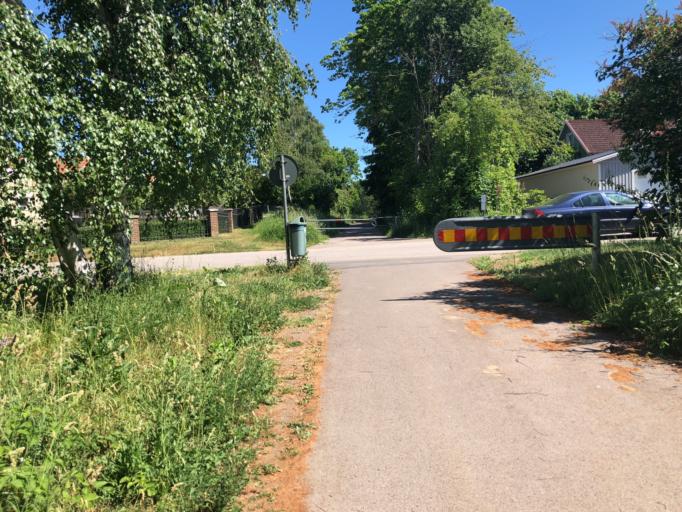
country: SE
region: Kalmar
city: Faerjestaden
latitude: 56.6296
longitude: 16.5106
